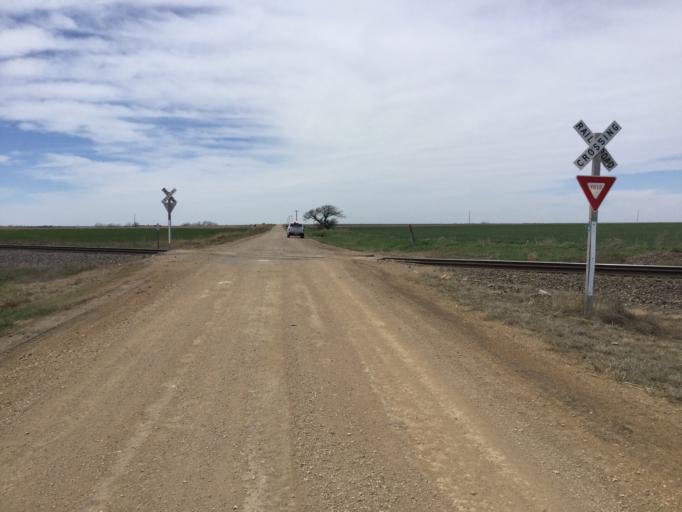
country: US
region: Kansas
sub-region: Russell County
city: Russell
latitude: 38.8709
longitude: -98.7396
